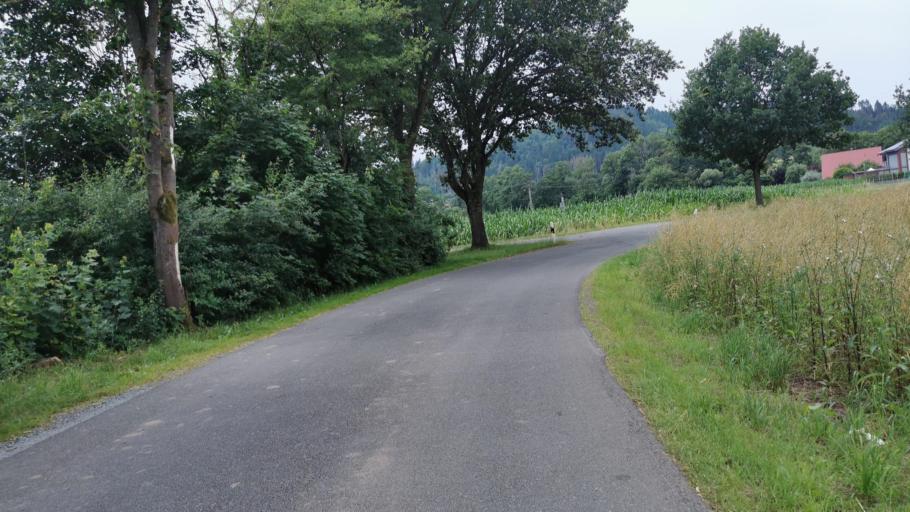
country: DE
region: Bavaria
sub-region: Upper Franconia
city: Stockheim
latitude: 50.3169
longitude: 11.2864
